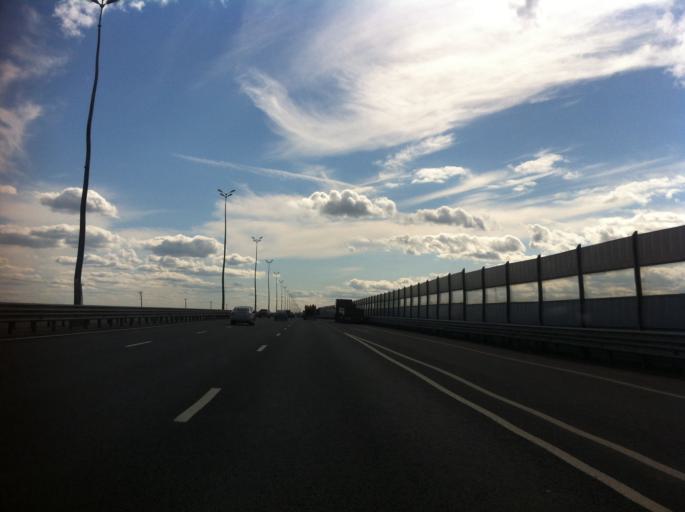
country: RU
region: Leningrad
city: Maloye Verevo
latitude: 59.6439
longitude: 30.2239
